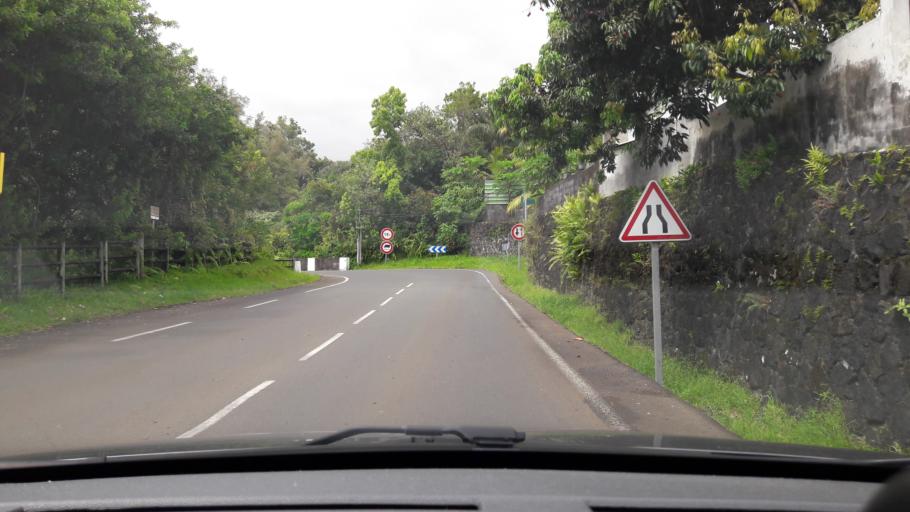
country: RE
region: Reunion
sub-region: Reunion
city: Saint-Benoit
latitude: -21.0846
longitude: 55.6952
